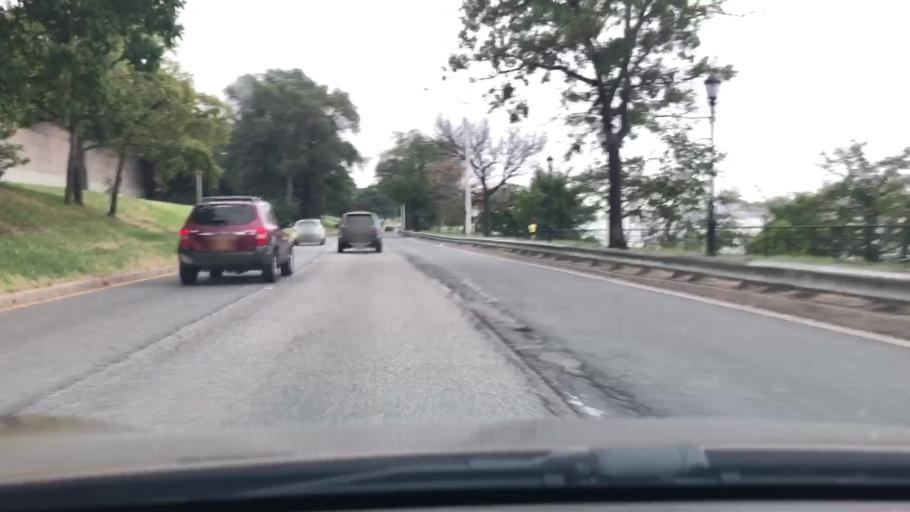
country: US
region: New Jersey
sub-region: Bergen County
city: Edgewater
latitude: 40.8150
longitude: -73.9645
